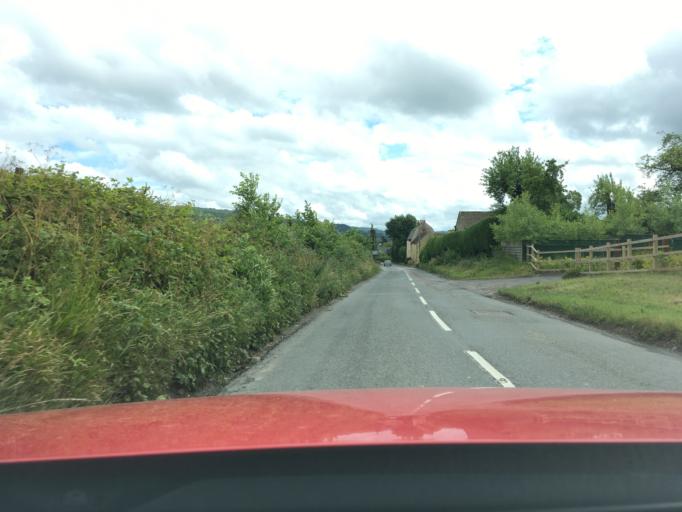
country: GB
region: England
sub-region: Gloucestershire
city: Winchcombe
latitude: 51.9698
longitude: -1.9670
